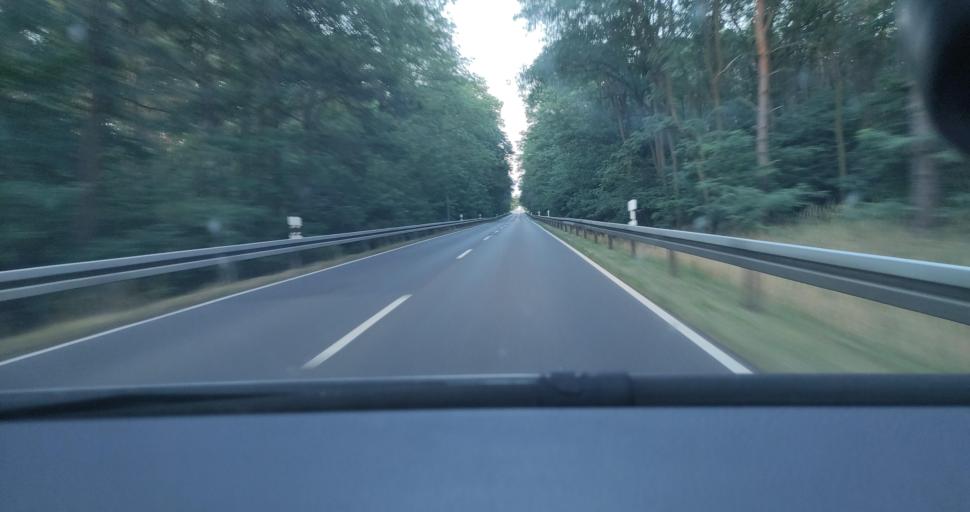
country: DE
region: Brandenburg
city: Heinersbruck
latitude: 51.7275
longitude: 14.5208
